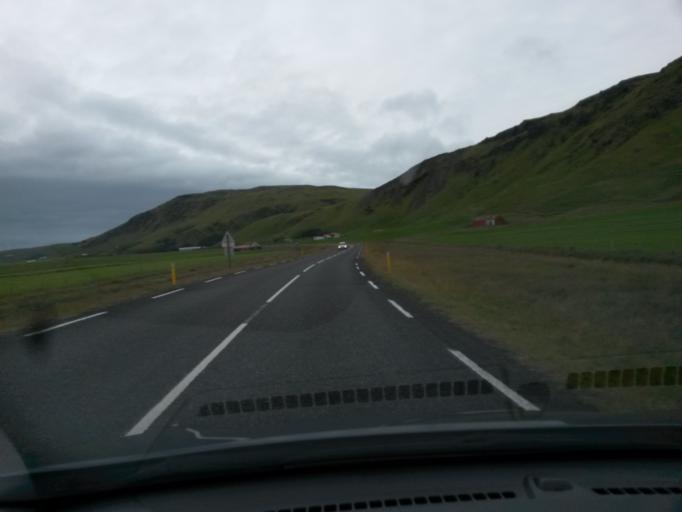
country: IS
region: South
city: Vestmannaeyjar
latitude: 63.4550
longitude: -19.0678
